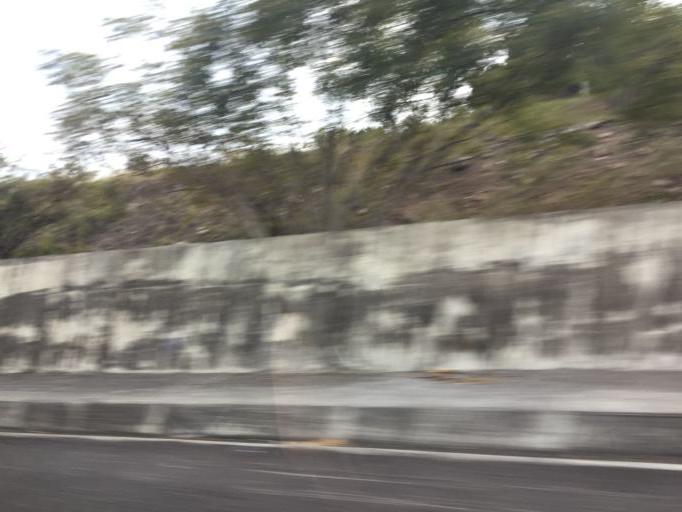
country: MX
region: Michoacan
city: Copandaro de Galeana
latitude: 19.8928
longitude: -101.2437
